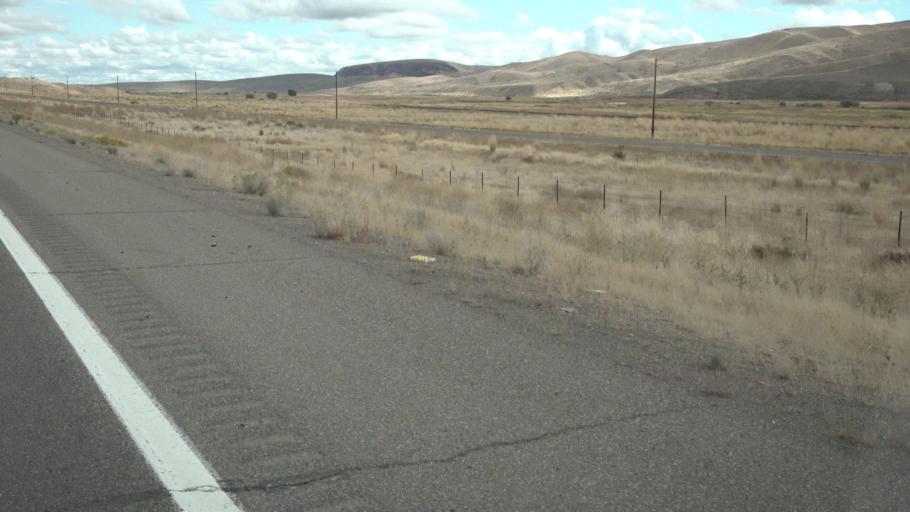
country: US
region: Nevada
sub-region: Elko County
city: Elko
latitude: 40.9212
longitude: -115.6842
